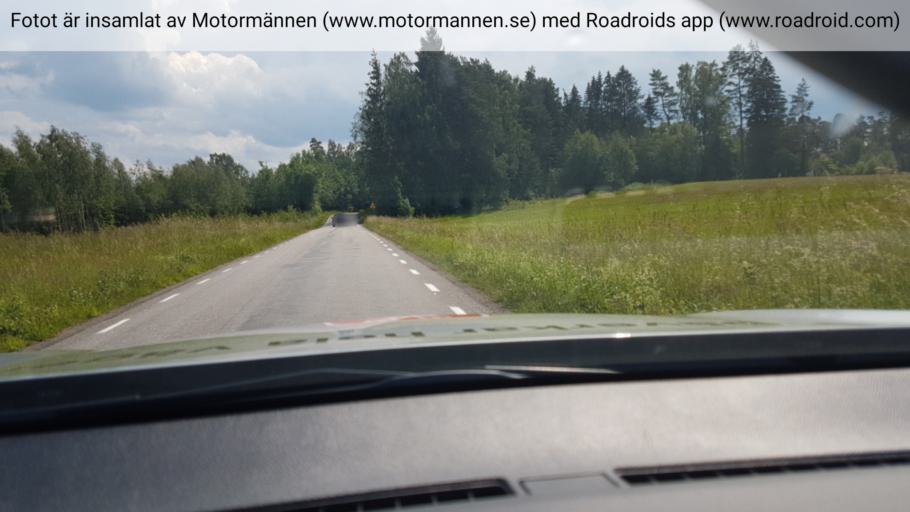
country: SE
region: Vaestra Goetaland
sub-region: Skara Kommun
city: Skara
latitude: 58.4391
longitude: 13.4026
